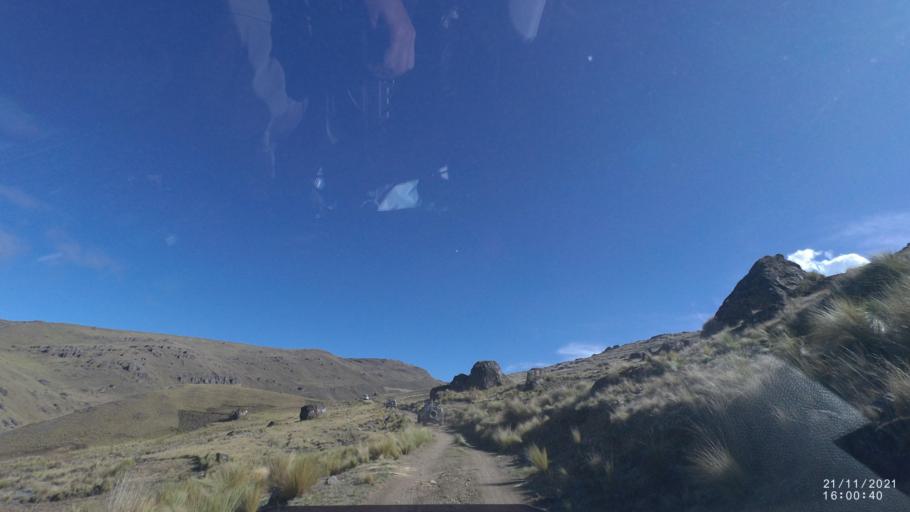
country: BO
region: Cochabamba
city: Cochabamba
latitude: -16.9817
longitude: -66.2619
